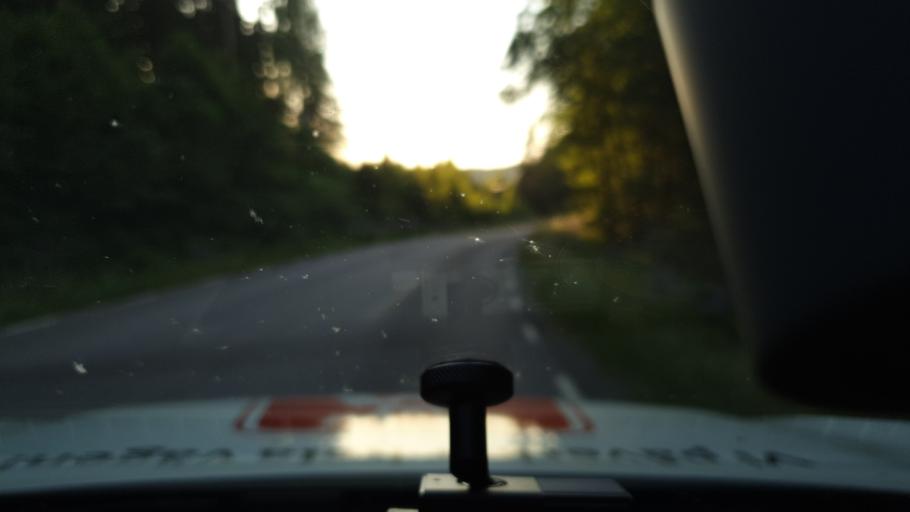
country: SE
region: Vaermland
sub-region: Kils Kommun
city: Kil
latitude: 59.6815
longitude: 13.2786
